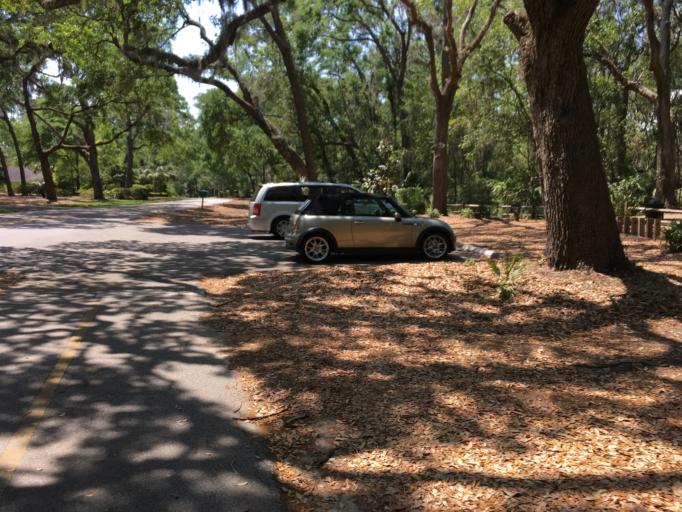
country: US
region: South Carolina
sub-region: Beaufort County
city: Hilton Head Island
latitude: 32.1290
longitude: -80.8133
